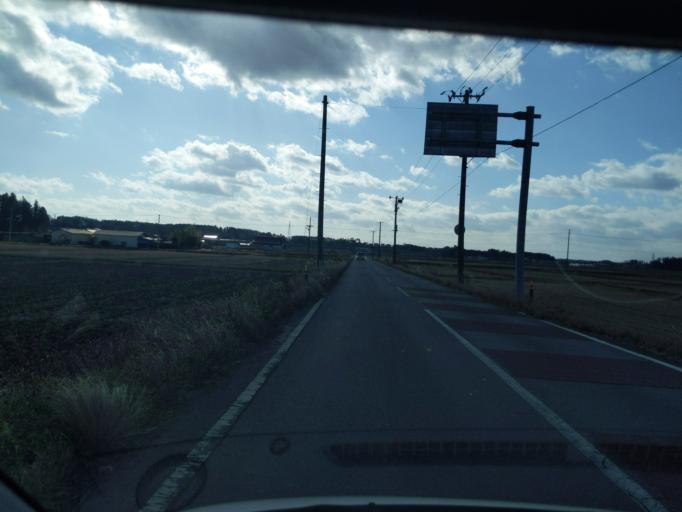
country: JP
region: Iwate
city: Ichinoseki
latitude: 38.7475
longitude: 141.0665
